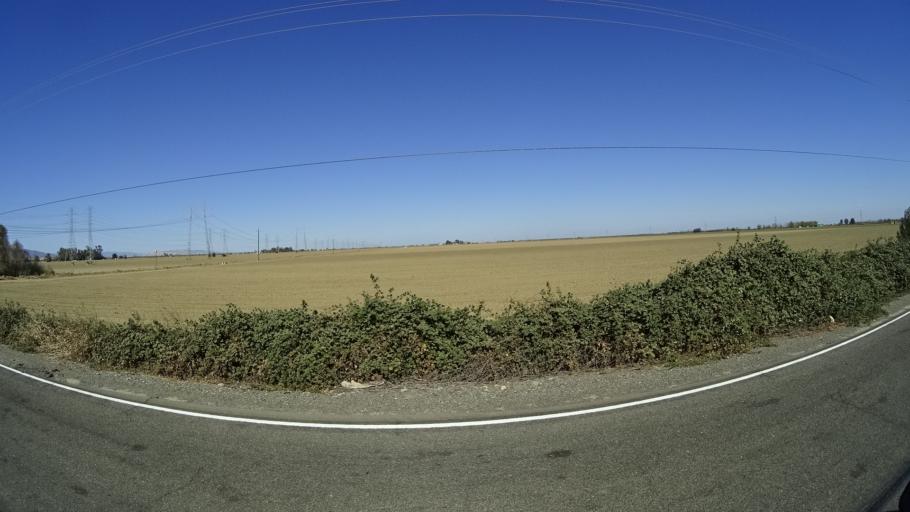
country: US
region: California
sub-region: Yolo County
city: Winters
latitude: 38.5620
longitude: -121.9242
